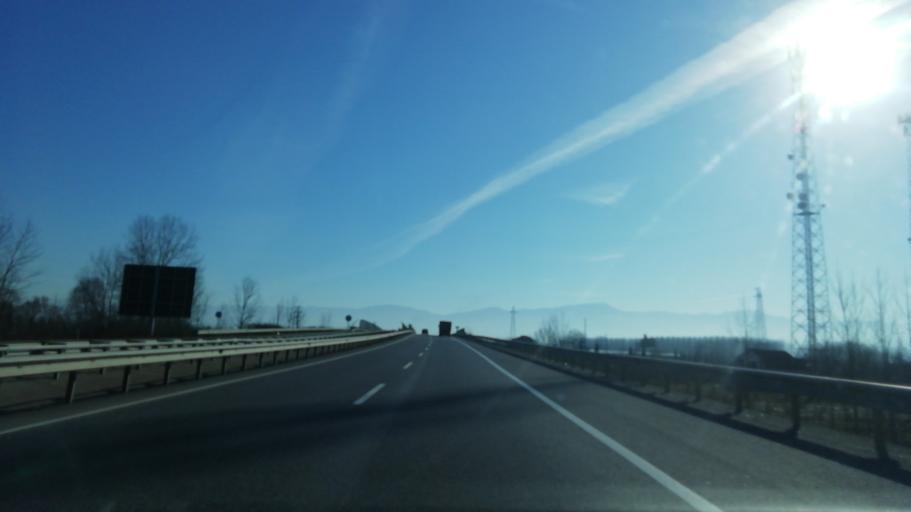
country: TR
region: Sakarya
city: Akyazi
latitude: 40.7191
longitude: 30.5632
